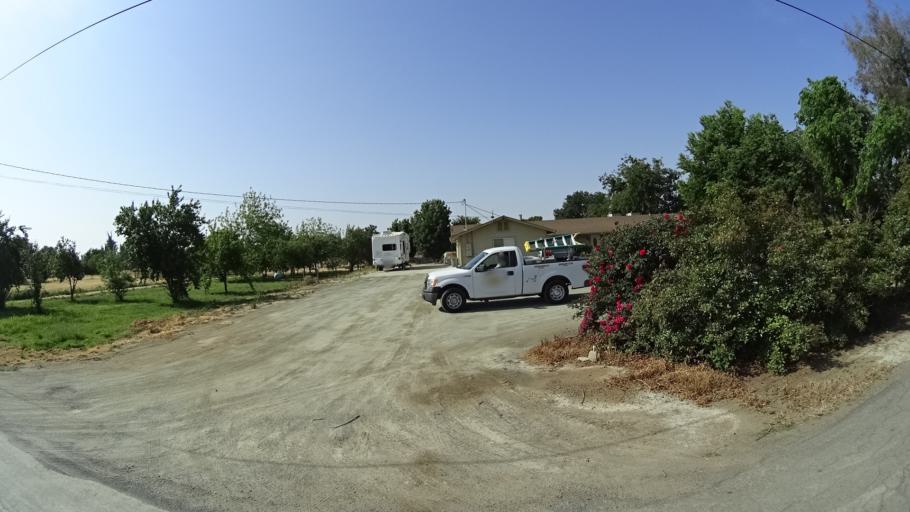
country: US
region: California
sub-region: Kings County
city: Lemoore
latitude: 36.3531
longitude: -119.8398
